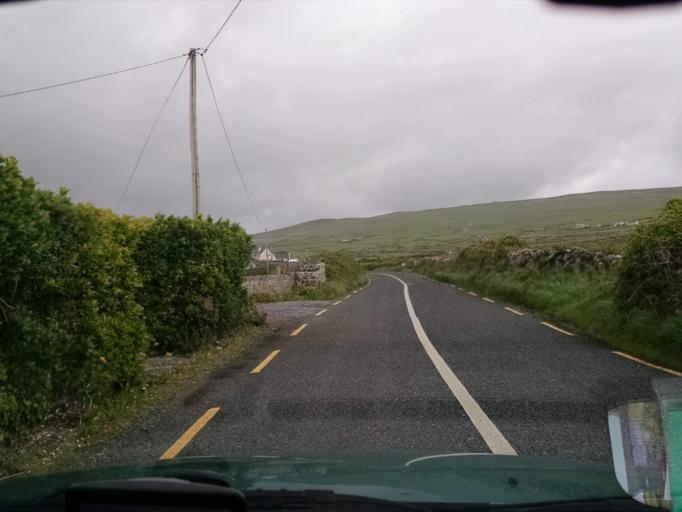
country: IE
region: Connaught
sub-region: County Galway
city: Bearna
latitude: 53.0981
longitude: -9.3011
